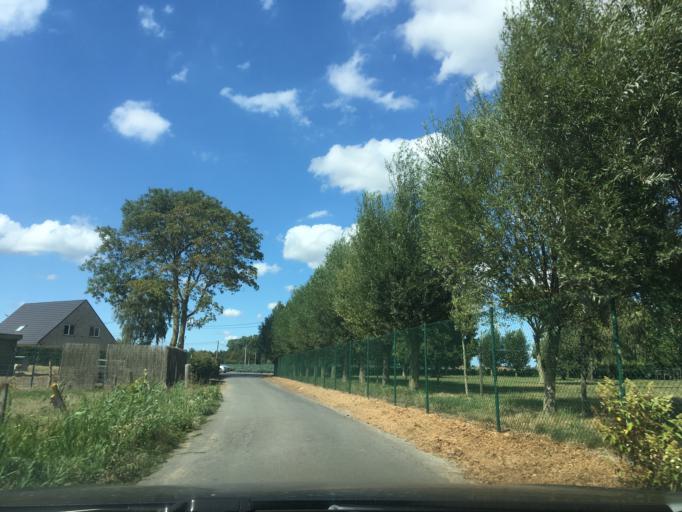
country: BE
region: Flanders
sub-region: Provincie West-Vlaanderen
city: Hooglede
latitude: 50.9726
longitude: 3.0538
